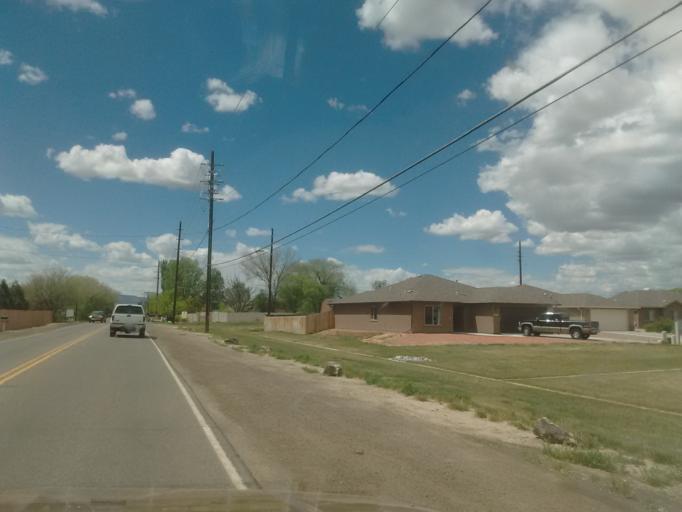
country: US
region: Colorado
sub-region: Mesa County
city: Clifton
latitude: 39.0773
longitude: -108.4676
